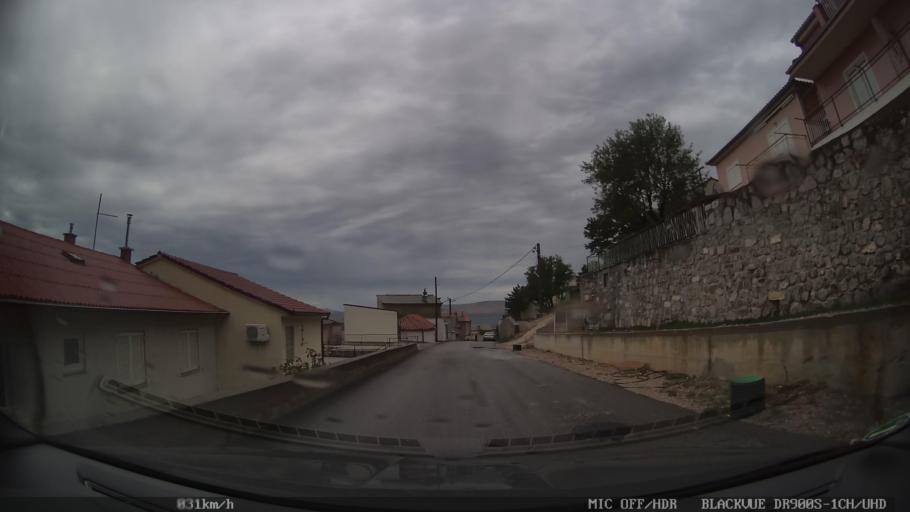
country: HR
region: Licko-Senjska
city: Senj
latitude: 44.9946
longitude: 14.9032
